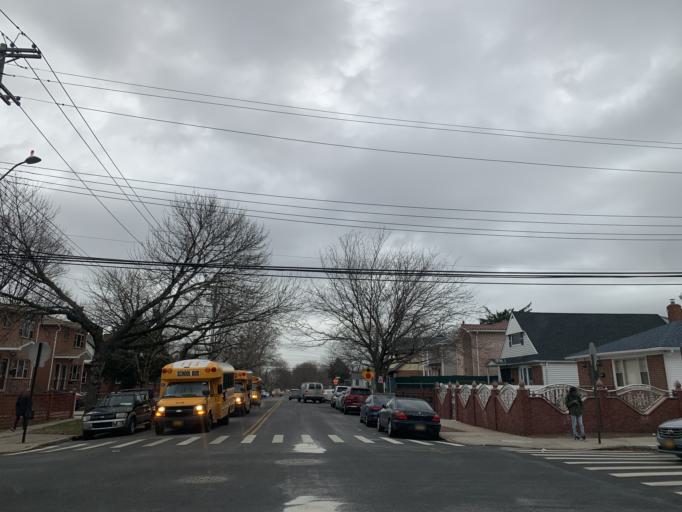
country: US
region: New York
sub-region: Queens County
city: Jamaica
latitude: 40.6822
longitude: -73.8009
